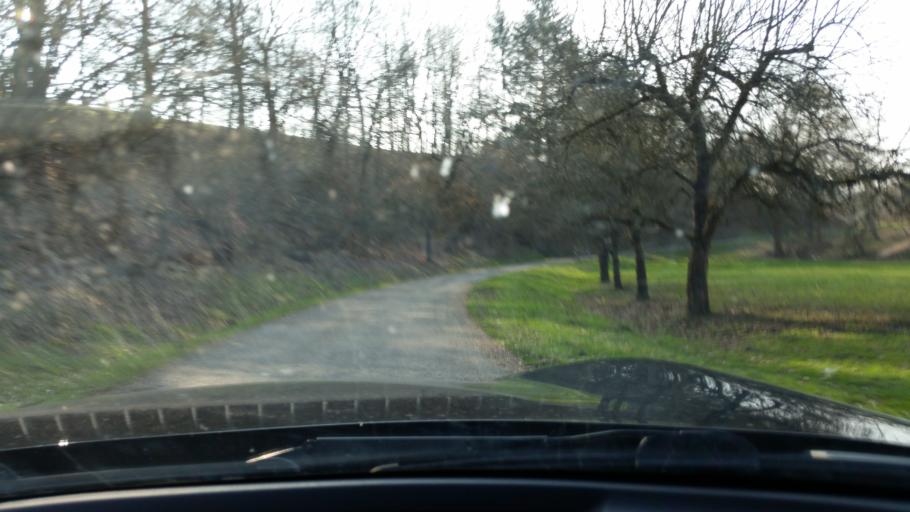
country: DE
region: Baden-Wuerttemberg
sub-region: Regierungsbezirk Stuttgart
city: Mockmuhl
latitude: 49.3175
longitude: 9.3883
